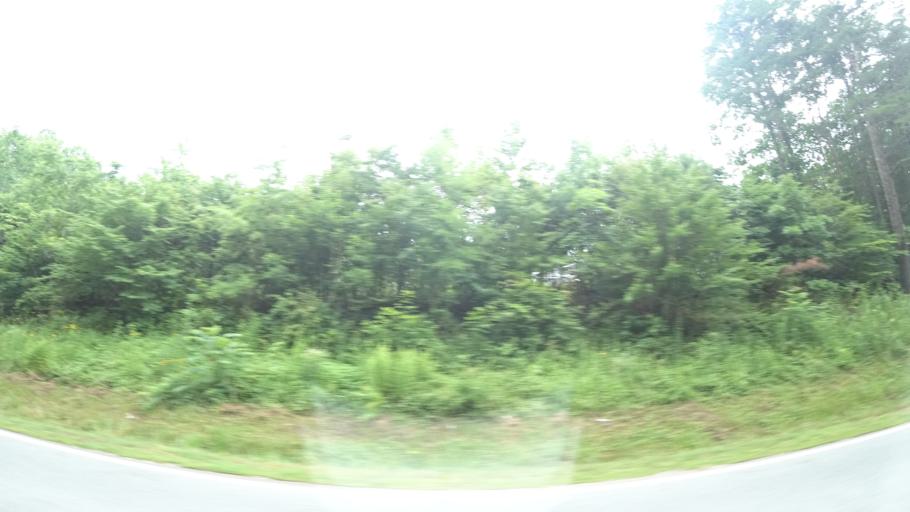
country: US
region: Virginia
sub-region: Spotsylvania County
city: Spotsylvania
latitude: 38.1383
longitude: -77.8025
